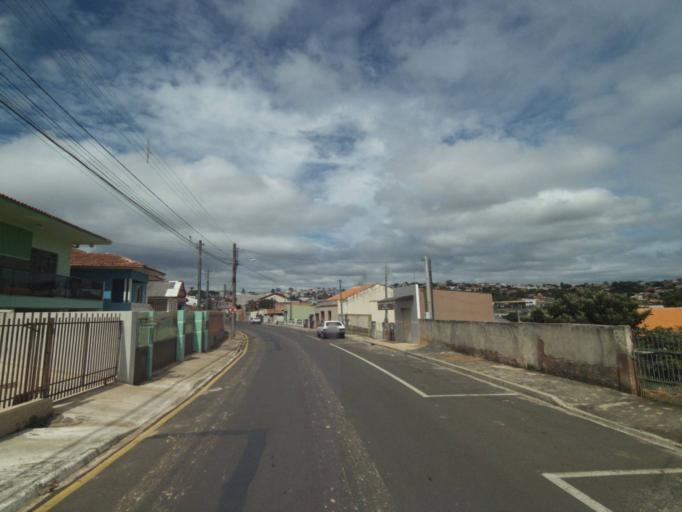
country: BR
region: Parana
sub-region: Telemaco Borba
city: Telemaco Borba
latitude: -24.3279
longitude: -50.6308
